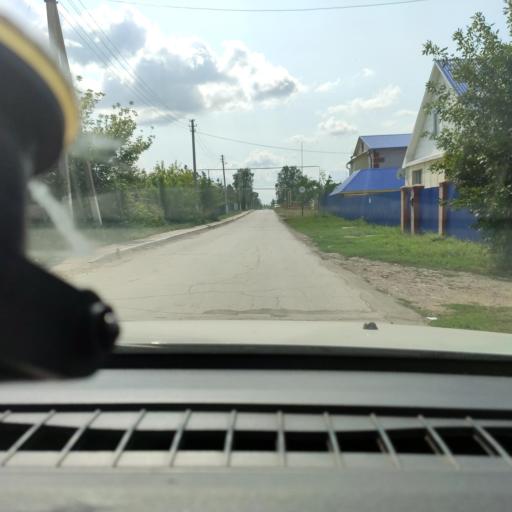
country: RU
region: Samara
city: Chapayevsk
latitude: 53.0137
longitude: 49.7480
